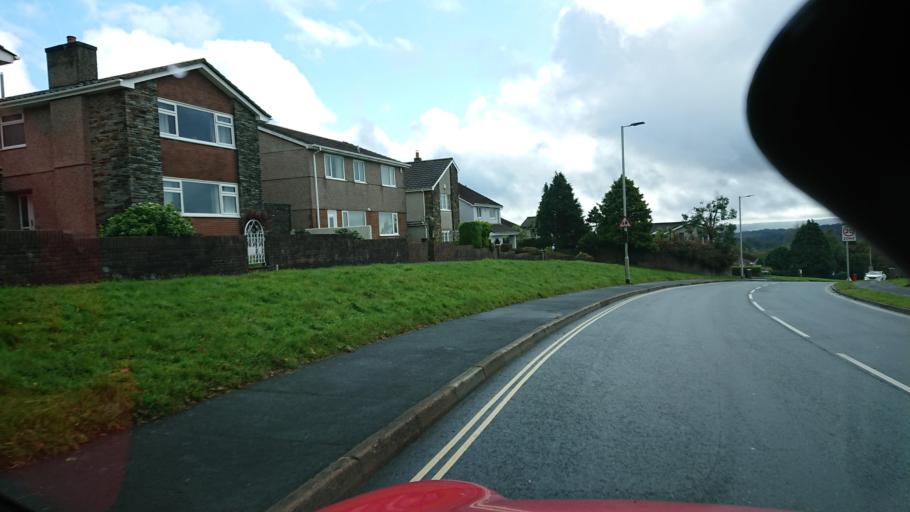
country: GB
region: England
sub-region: Devon
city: Plympton
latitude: 50.4190
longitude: -4.1023
